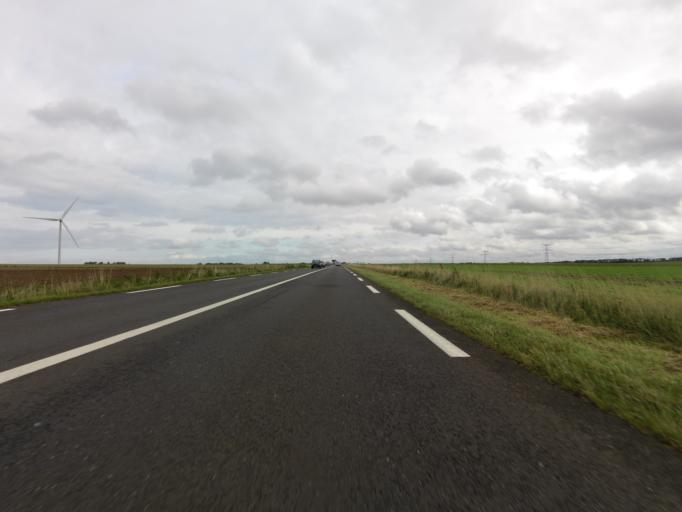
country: FR
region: Haute-Normandie
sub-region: Departement de la Seine-Maritime
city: Le Treport
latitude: 50.0196
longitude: 1.3645
